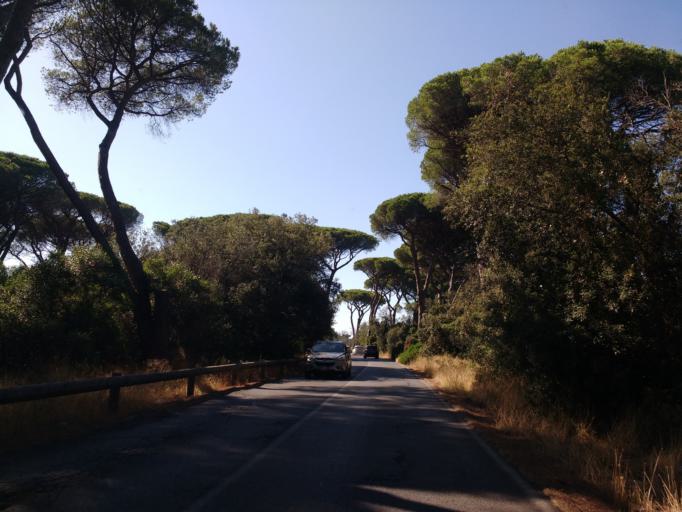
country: IT
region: Latium
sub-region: Citta metropolitana di Roma Capitale
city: Acilia-Castel Fusano-Ostia Antica
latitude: 41.7242
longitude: 12.3437
